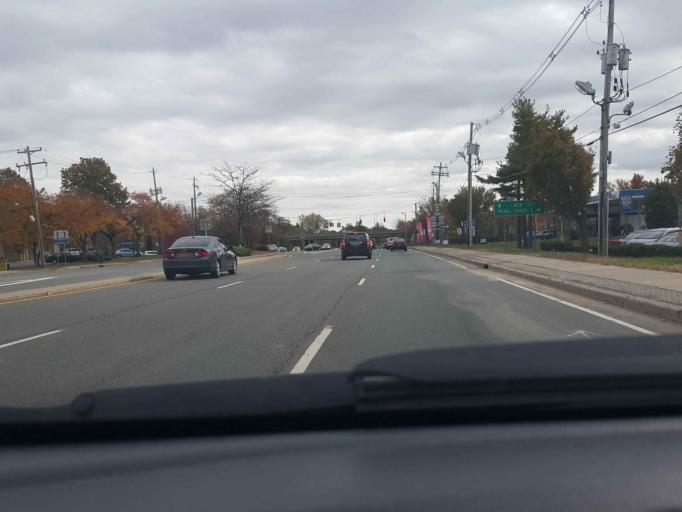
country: US
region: New York
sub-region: Rockland County
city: Nanuet
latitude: 41.0931
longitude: -74.0015
